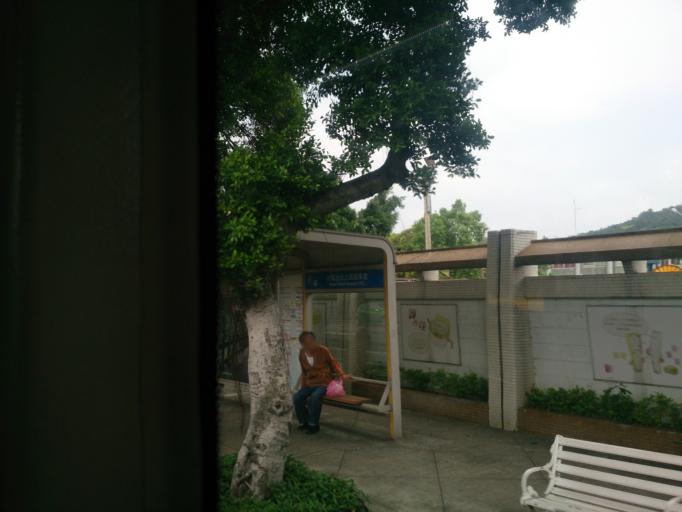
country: TW
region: Taipei
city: Taipei
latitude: 25.0911
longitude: 121.5277
